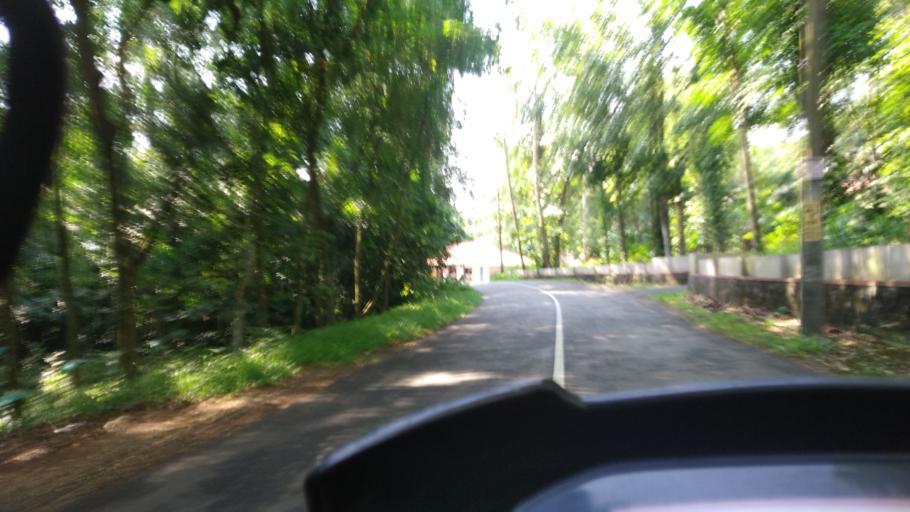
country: IN
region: Kerala
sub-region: Kottayam
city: Palackattumala
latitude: 9.7970
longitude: 76.5893
